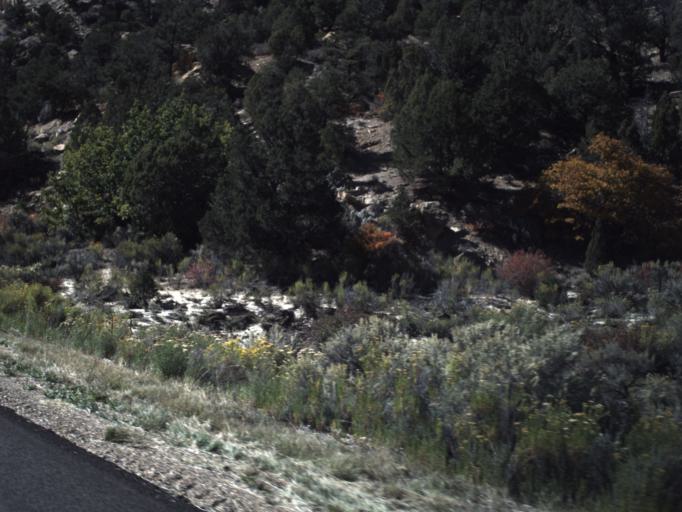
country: US
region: Utah
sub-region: Garfield County
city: Panguitch
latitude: 37.6096
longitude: -111.9011
